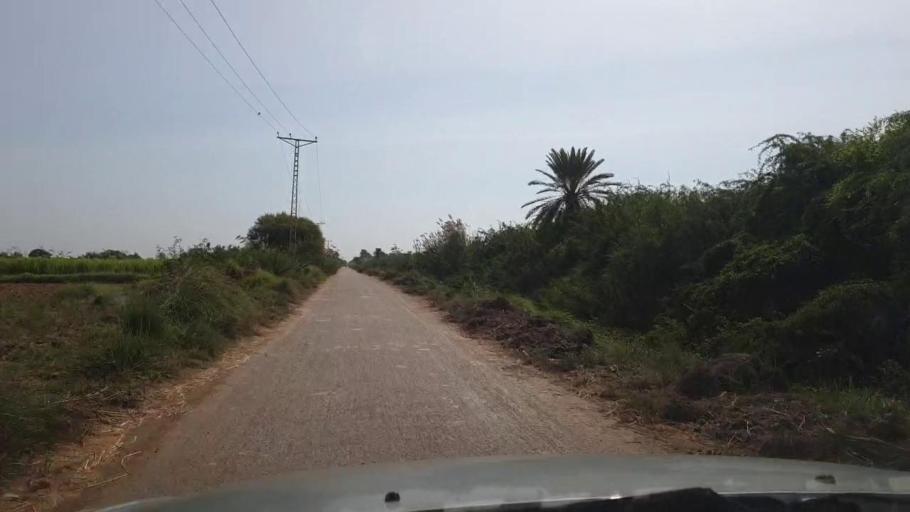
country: PK
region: Sindh
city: Tando Muhammad Khan
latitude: 25.1558
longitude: 68.3802
